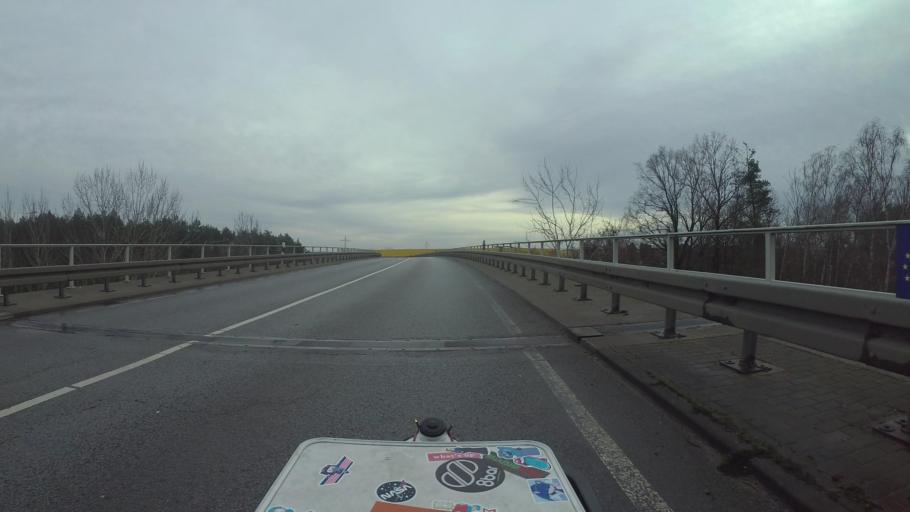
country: DE
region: Brandenburg
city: Ludwigsfelde
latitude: 52.3296
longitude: 13.2753
